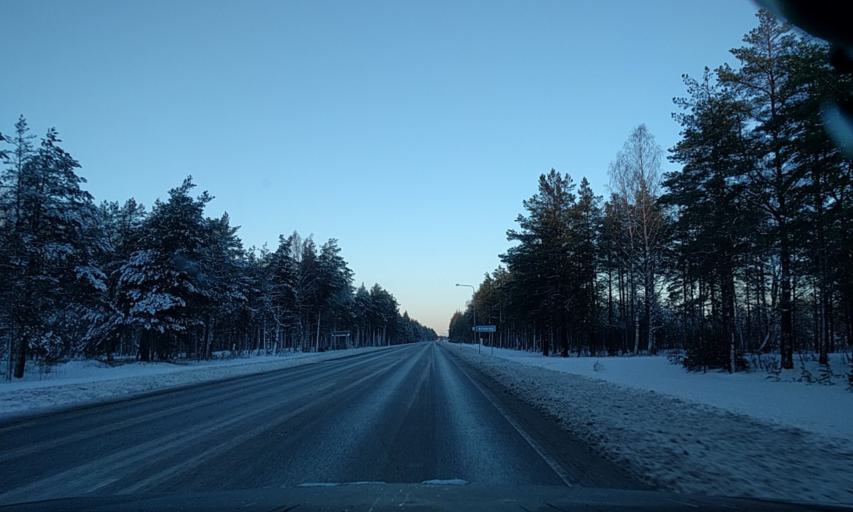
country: EE
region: Harju
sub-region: Saku vald
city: Saku
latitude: 59.3235
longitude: 24.6898
